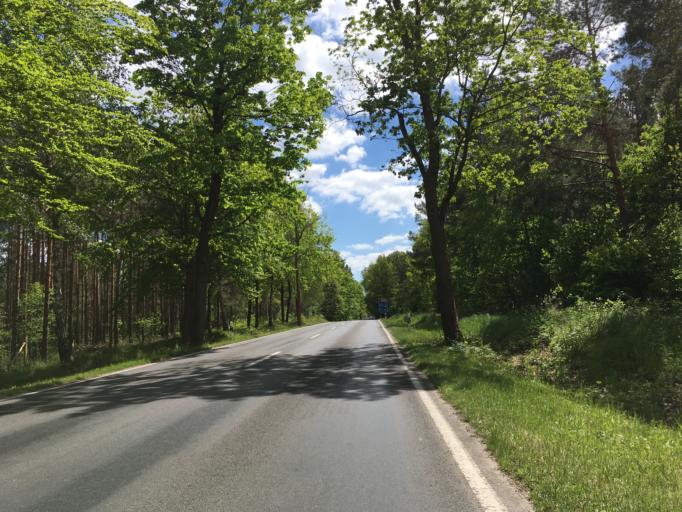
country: DE
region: Brandenburg
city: Marienwerder
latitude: 52.7773
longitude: 13.5595
